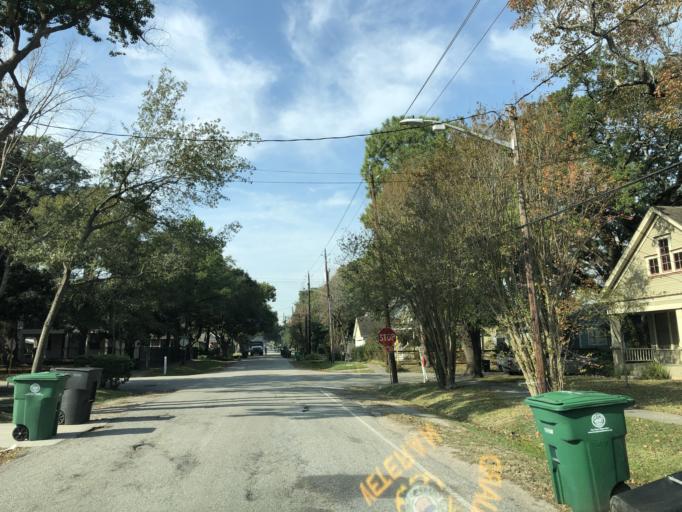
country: US
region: Texas
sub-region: Harris County
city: Houston
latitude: 29.7943
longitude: -95.4007
